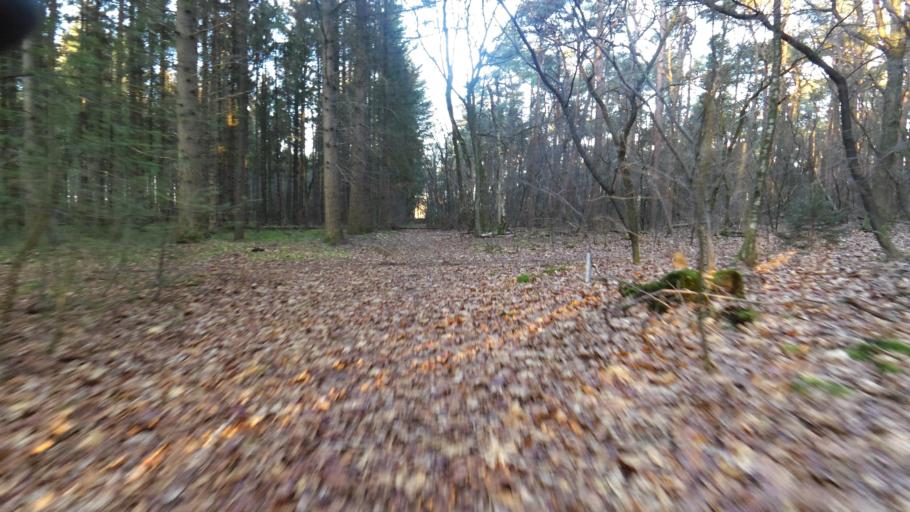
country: NL
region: Gelderland
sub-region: Gemeente Barneveld
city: Garderen
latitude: 52.2154
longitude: 5.7518
